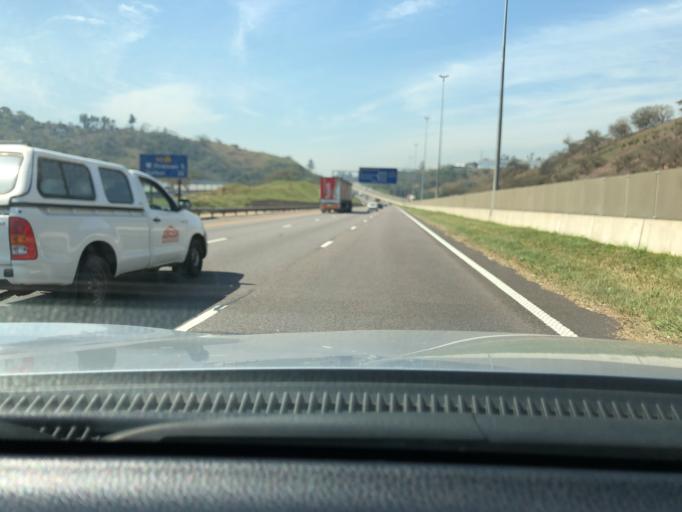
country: ZA
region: KwaZulu-Natal
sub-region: eThekwini Metropolitan Municipality
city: Berea
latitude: -29.8268
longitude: 30.8194
